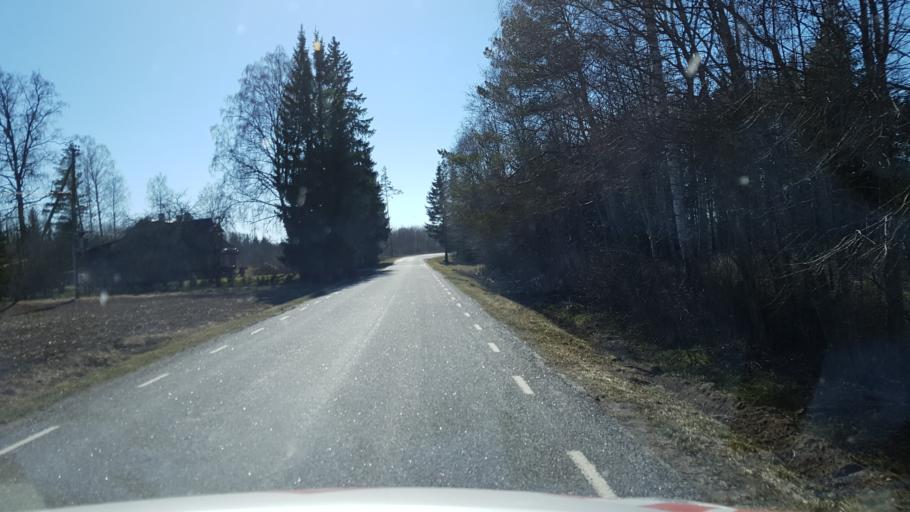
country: EE
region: Laeaene-Virumaa
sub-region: Tamsalu vald
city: Tamsalu
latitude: 59.0791
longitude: 26.1479
